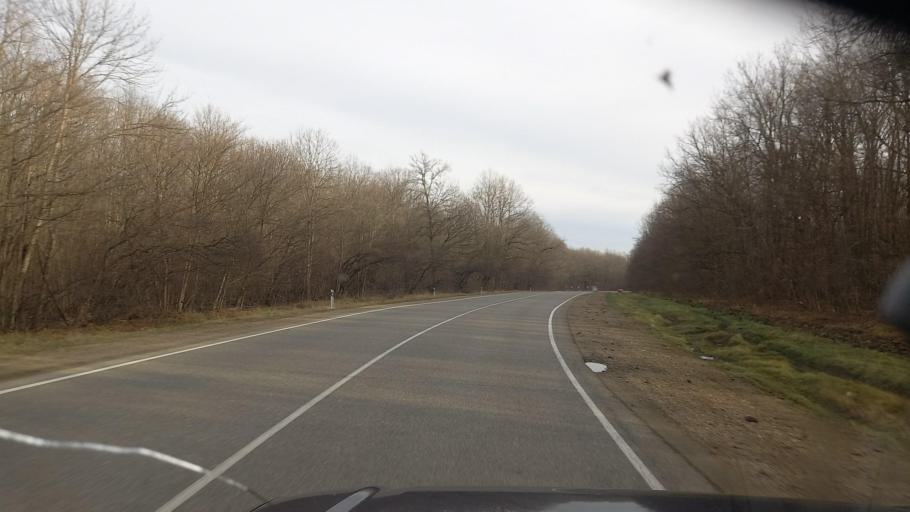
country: RU
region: Krasnodarskiy
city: Khadyzhensk
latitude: 44.6375
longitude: 39.5129
